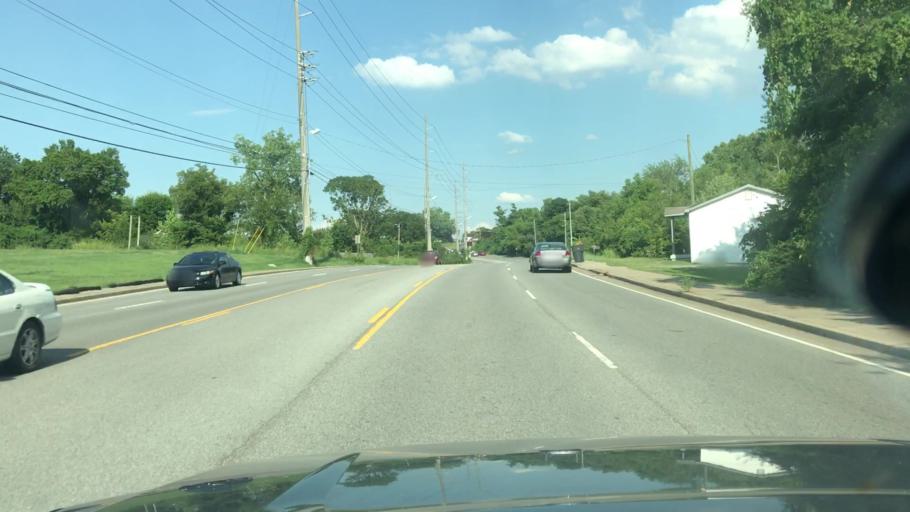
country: US
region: Tennessee
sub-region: Davidson County
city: Nashville
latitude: 36.2070
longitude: -86.7957
